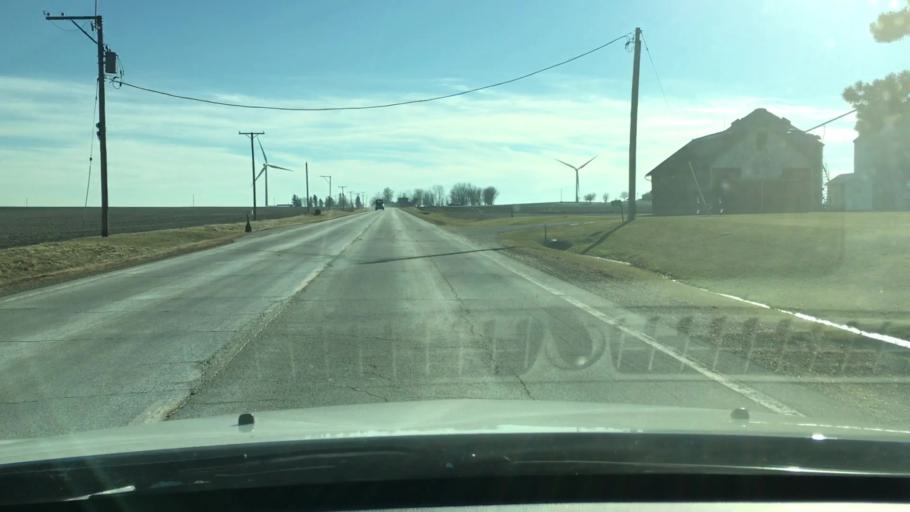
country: US
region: Illinois
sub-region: LaSalle County
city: Mendota
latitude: 41.6333
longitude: -89.1295
